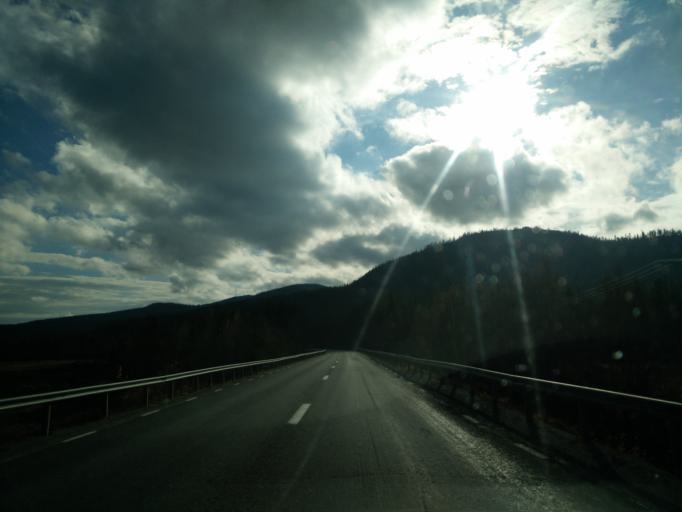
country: NO
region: Hedmark
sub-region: Engerdal
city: Engerdal
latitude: 62.4328
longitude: 12.7147
